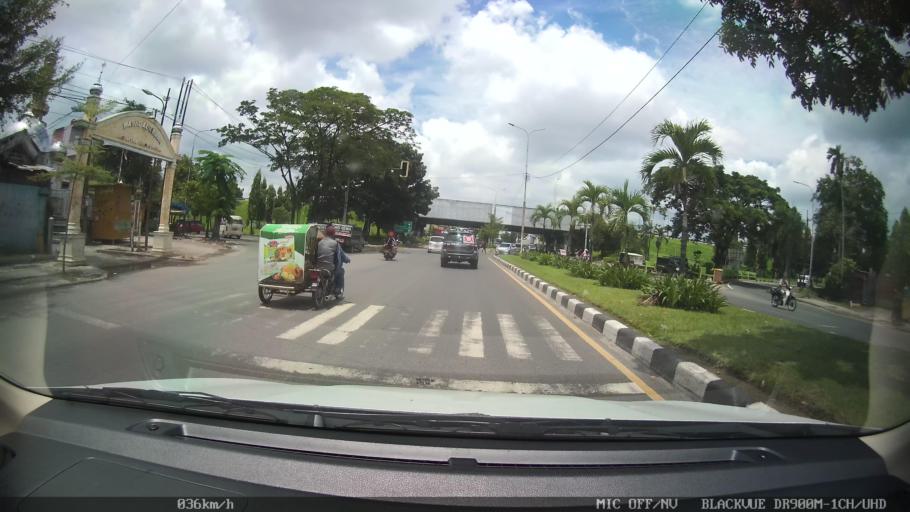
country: ID
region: North Sumatra
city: Medan
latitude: 3.5973
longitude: 98.7250
